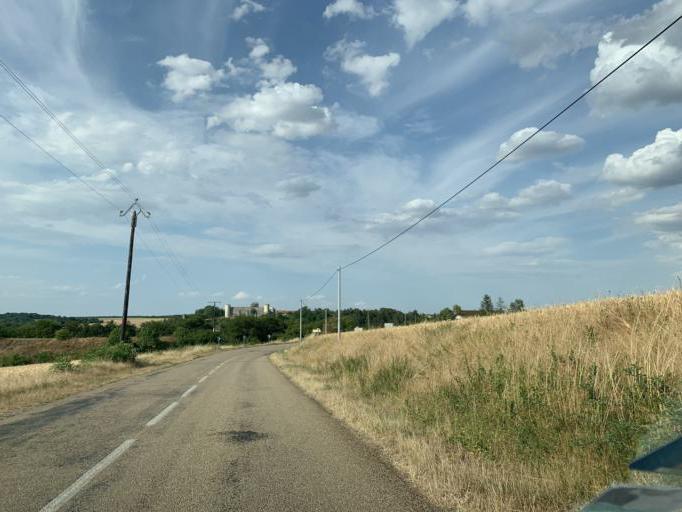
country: FR
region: Bourgogne
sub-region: Departement de l'Yonne
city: Fontenailles
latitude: 47.5425
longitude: 3.4182
